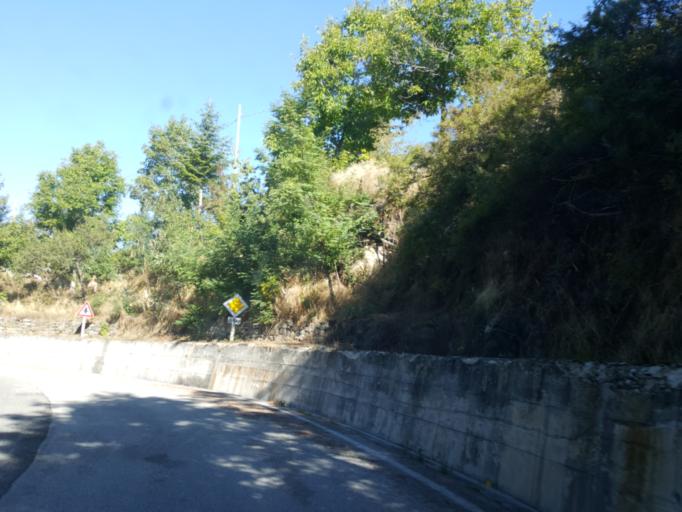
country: IT
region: Abruzzo
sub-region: Provincia dell' Aquila
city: Campotosto
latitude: 42.5576
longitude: 13.3662
